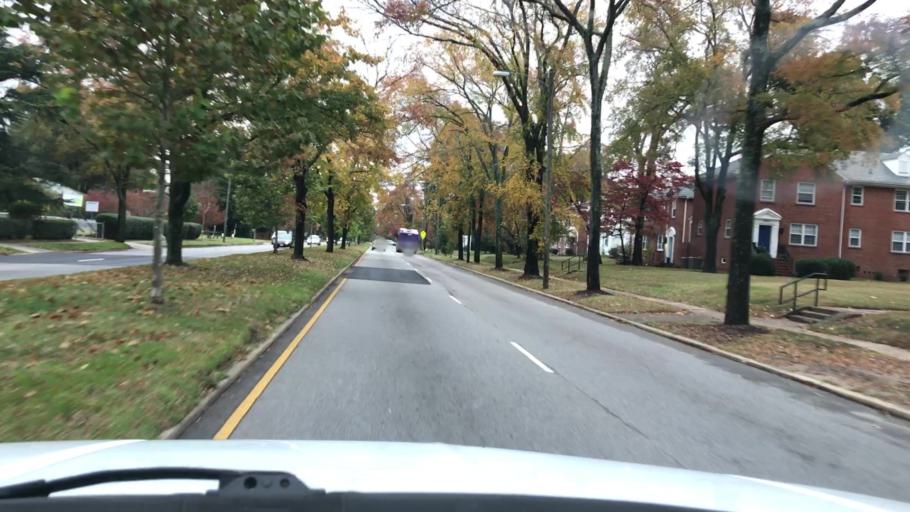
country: US
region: Virginia
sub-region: Henrico County
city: Lakeside
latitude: 37.5920
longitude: -77.4485
